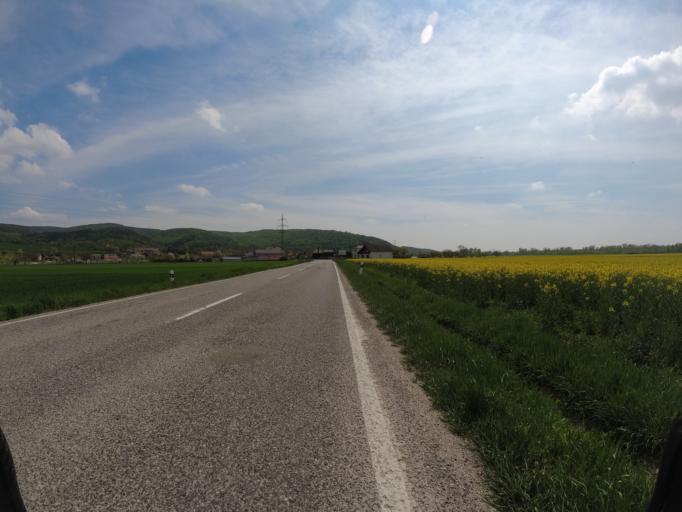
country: SK
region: Trnavsky
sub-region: Okres Trnava
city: Piestany
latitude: 48.5128
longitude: 17.8246
